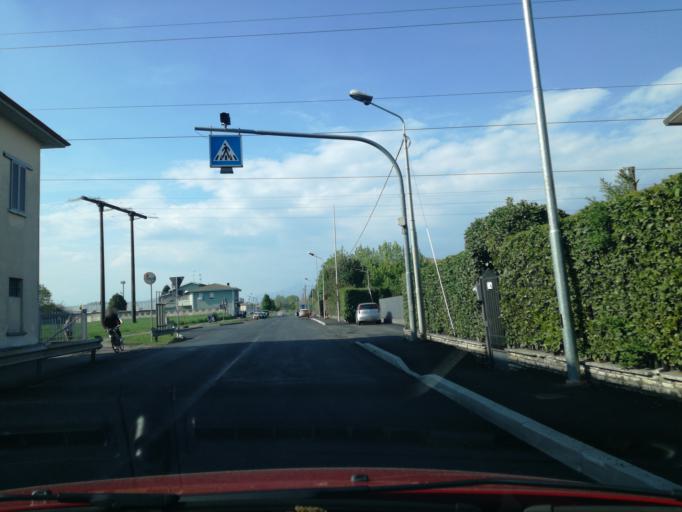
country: IT
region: Lombardy
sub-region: Provincia di Monza e Brianza
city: Cornate d'Adda
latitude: 45.6359
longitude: 9.4716
